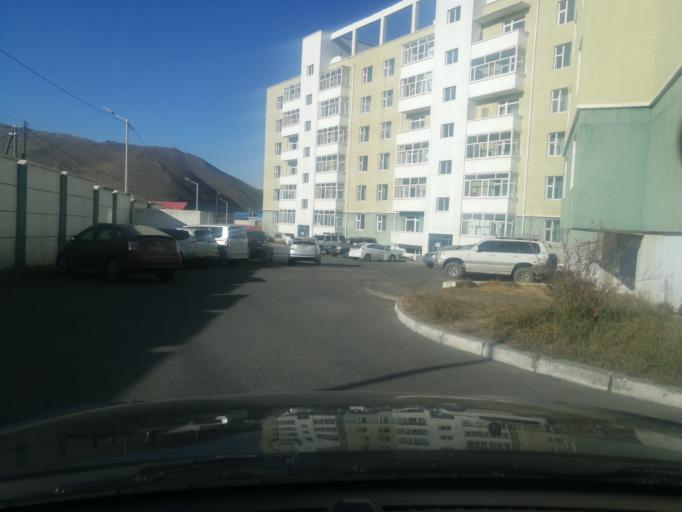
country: MN
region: Ulaanbaatar
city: Ulaanbaatar
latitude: 47.8870
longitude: 106.9035
